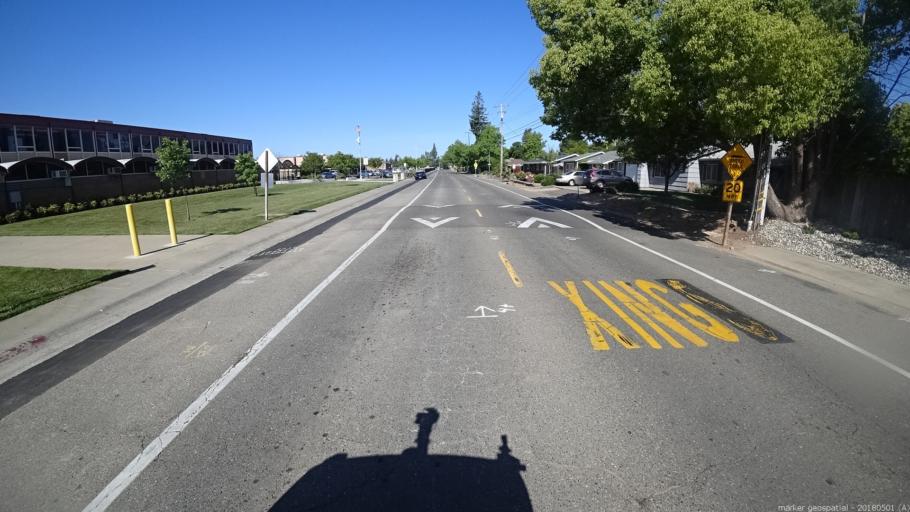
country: US
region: California
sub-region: Sacramento County
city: Arden-Arcade
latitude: 38.6342
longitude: -121.3698
